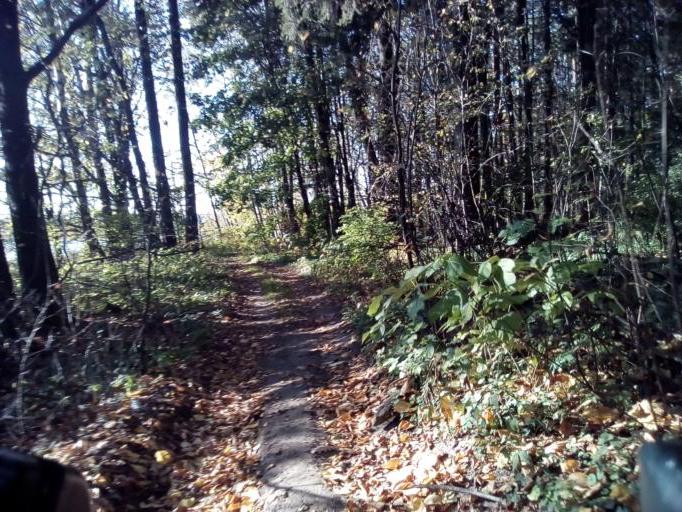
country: RU
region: Moskovskaya
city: Ramenskoye
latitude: 55.5758
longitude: 38.3131
